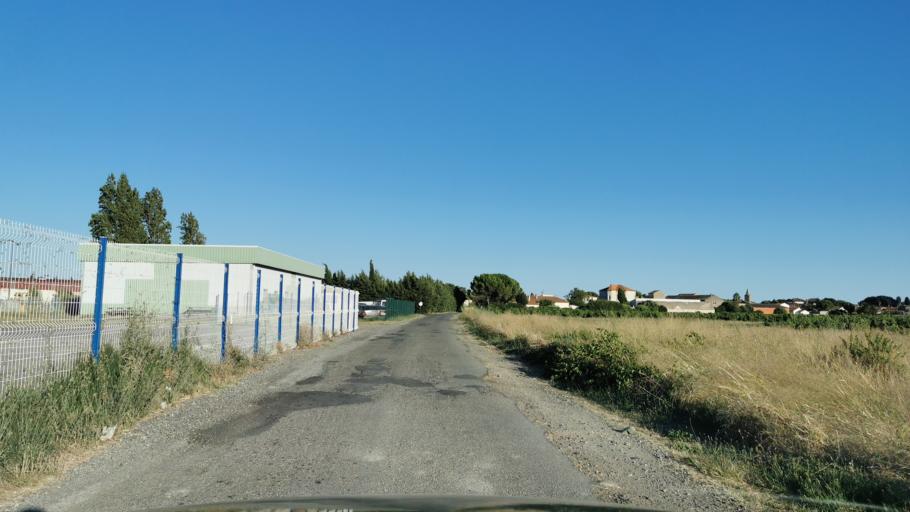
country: FR
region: Languedoc-Roussillon
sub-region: Departement de l'Aude
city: Ouveillan
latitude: 43.2524
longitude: 2.9945
